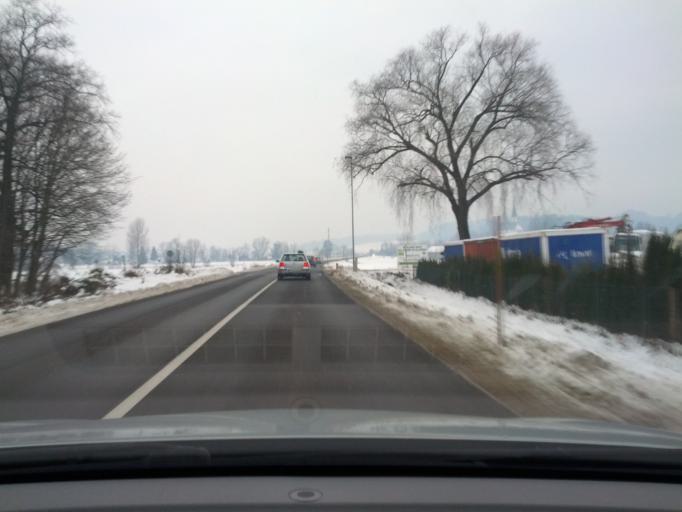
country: SI
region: Domzale
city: Dob
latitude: 46.1456
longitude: 14.6636
